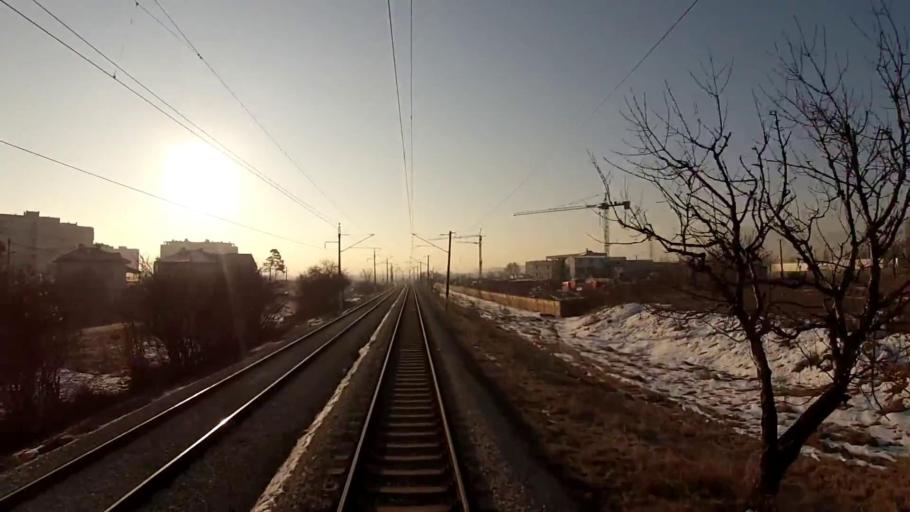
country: BG
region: Sofiya
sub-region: Obshtina Bozhurishte
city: Bozhurishte
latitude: 42.7455
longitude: 23.2560
